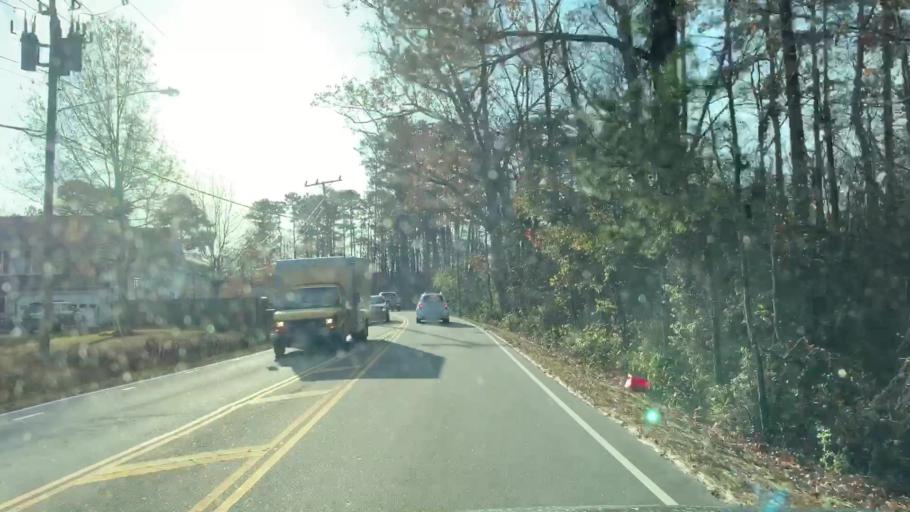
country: US
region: Virginia
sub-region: City of Chesapeake
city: Chesapeake
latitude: 36.7627
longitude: -76.1481
